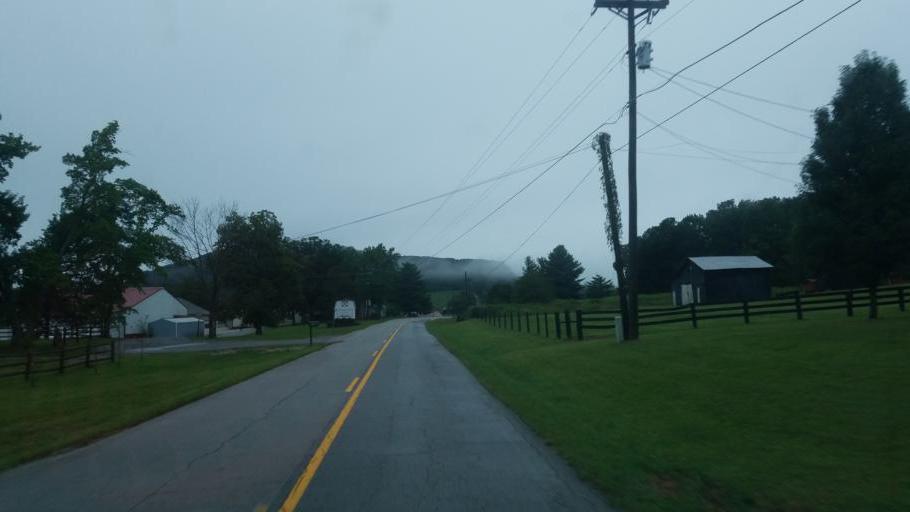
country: US
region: Kentucky
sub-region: Fleming County
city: Flemingsburg
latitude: 38.4044
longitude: -83.6377
